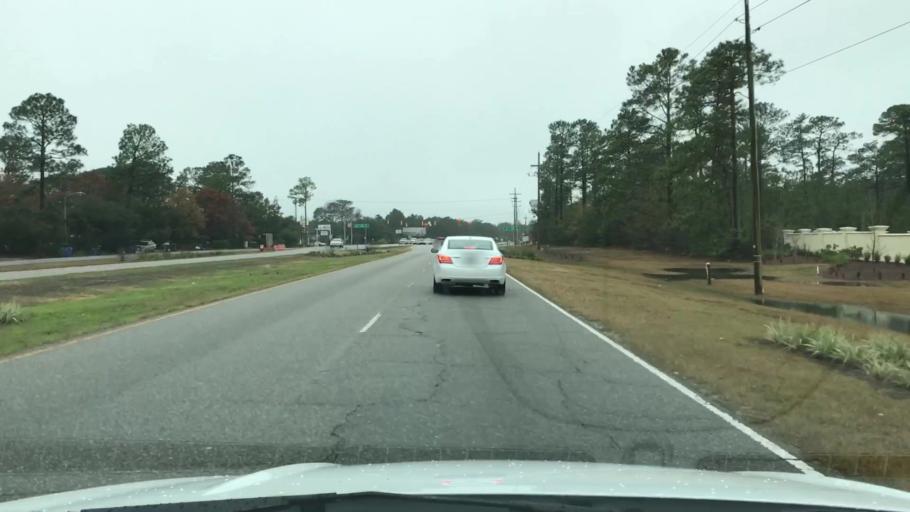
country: US
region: South Carolina
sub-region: Horry County
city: Myrtle Beach
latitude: 33.7452
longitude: -78.8387
